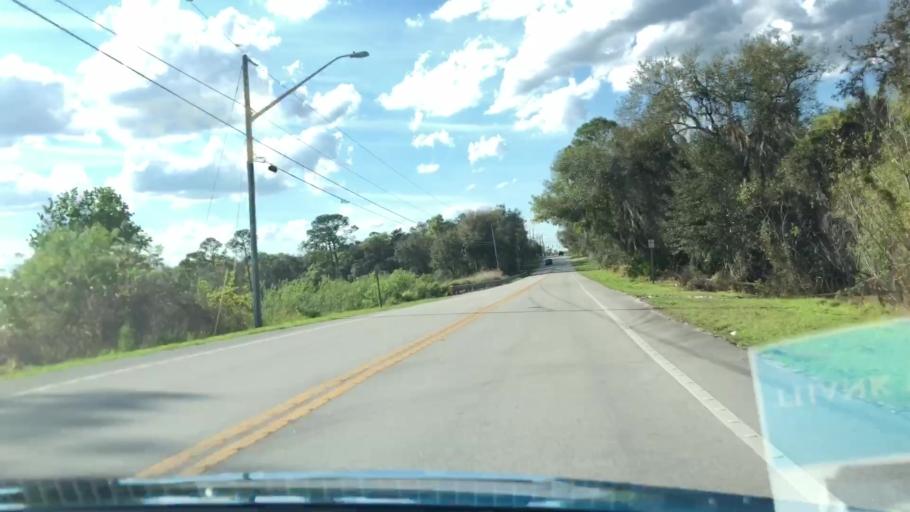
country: US
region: Florida
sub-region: Volusia County
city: Deltona
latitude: 28.8664
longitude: -81.2198
